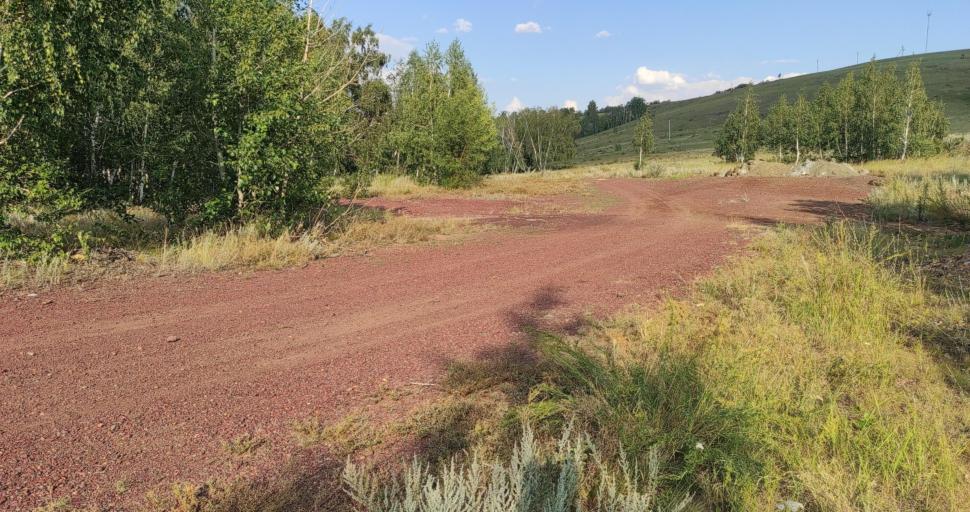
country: RU
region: Bashkortostan
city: Baymak
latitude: 52.5948
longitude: 58.4623
